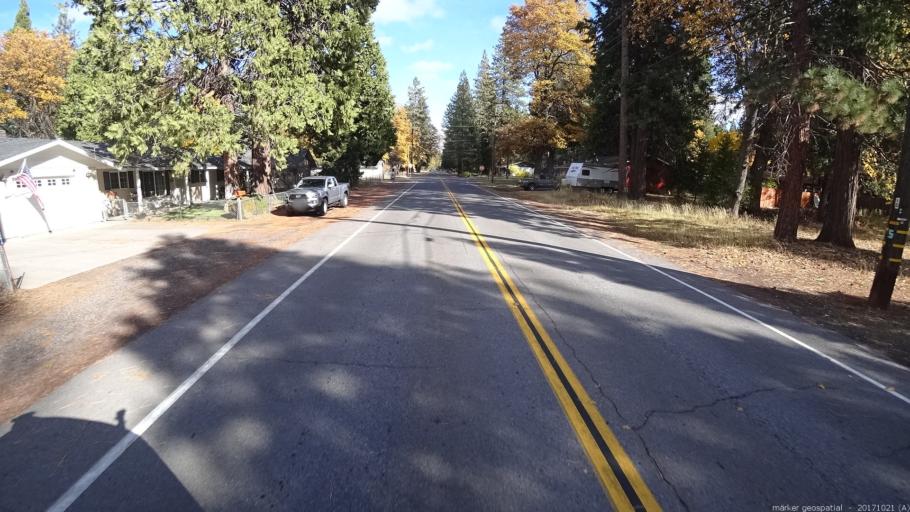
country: US
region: California
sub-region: Shasta County
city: Burney
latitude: 40.8768
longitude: -121.6583
